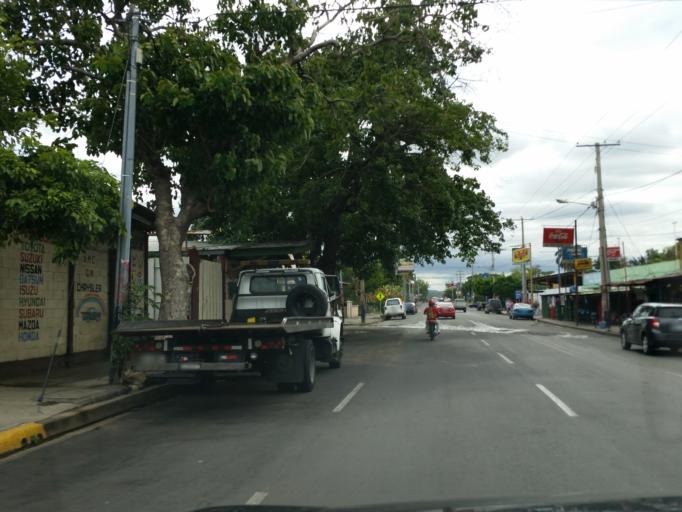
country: NI
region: Managua
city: Managua
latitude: 12.1470
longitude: -86.2828
